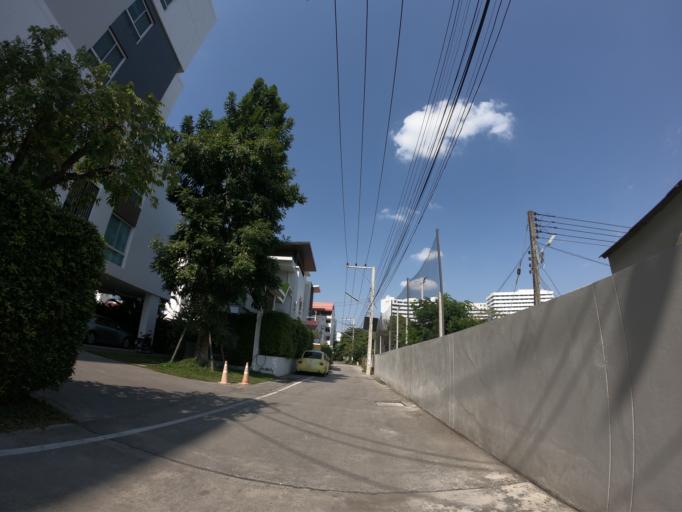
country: TH
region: Chiang Mai
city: Chiang Mai
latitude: 18.7869
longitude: 98.9739
